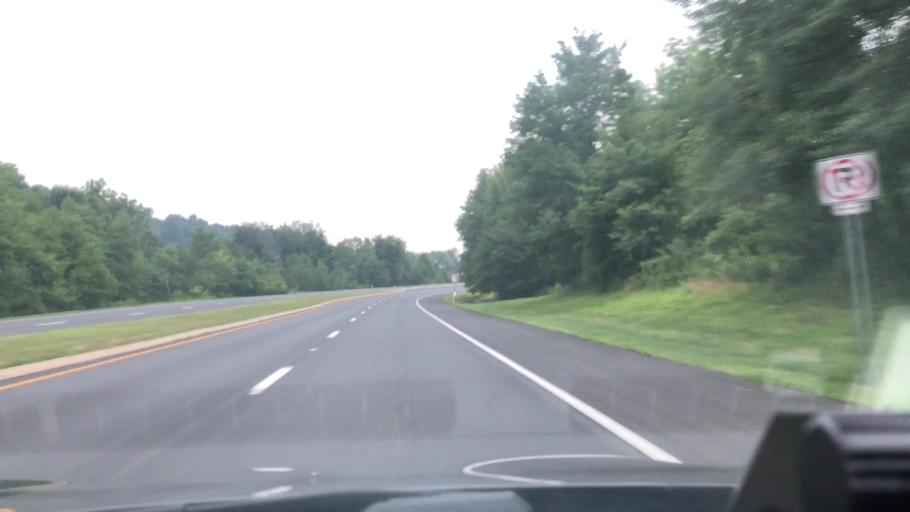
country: US
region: Pennsylvania
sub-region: Lehigh County
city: Fountain Hill
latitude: 40.5658
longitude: -75.3986
